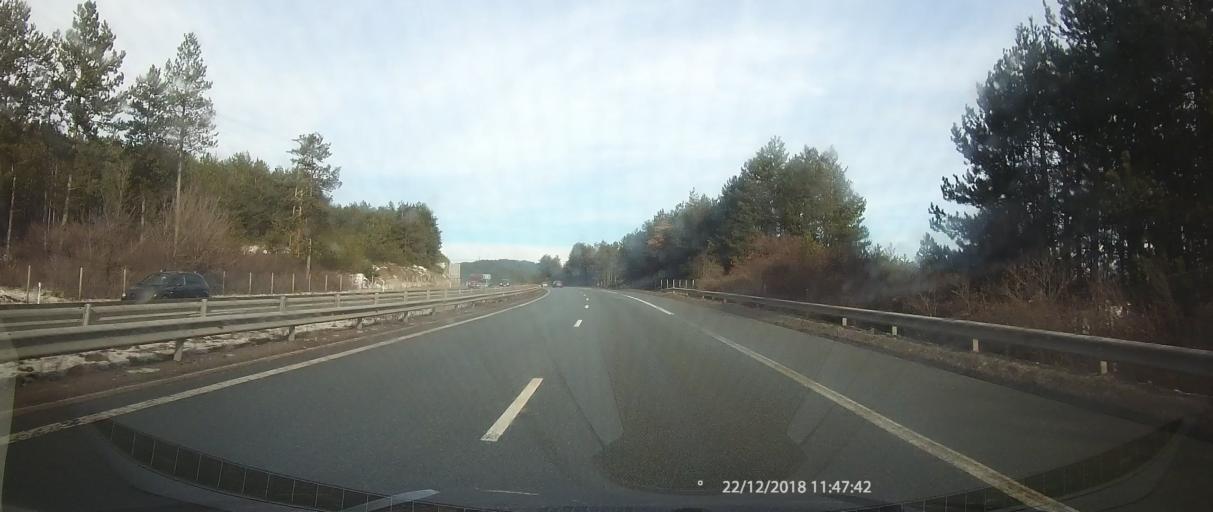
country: BG
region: Pernik
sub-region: Obshtina Pernik
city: Pernik
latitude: 42.5060
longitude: 23.1411
